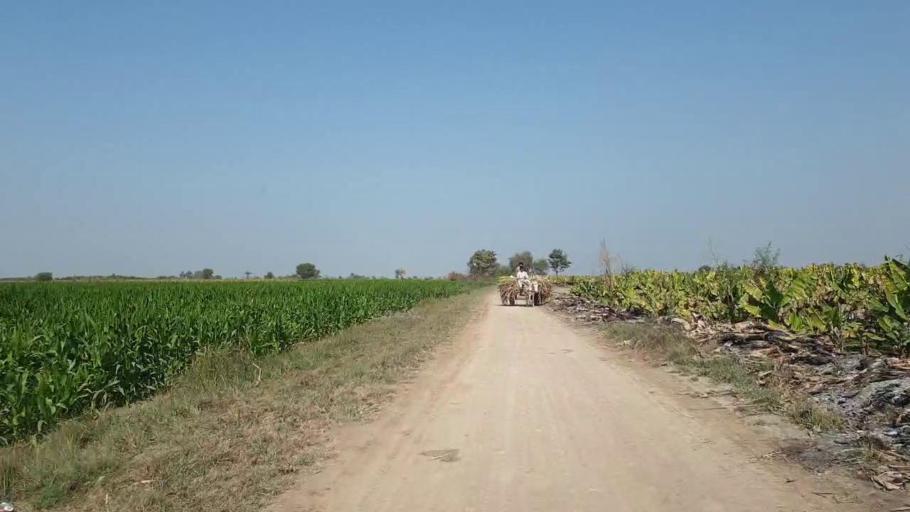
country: PK
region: Sindh
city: Hala
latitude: 25.9650
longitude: 68.4333
